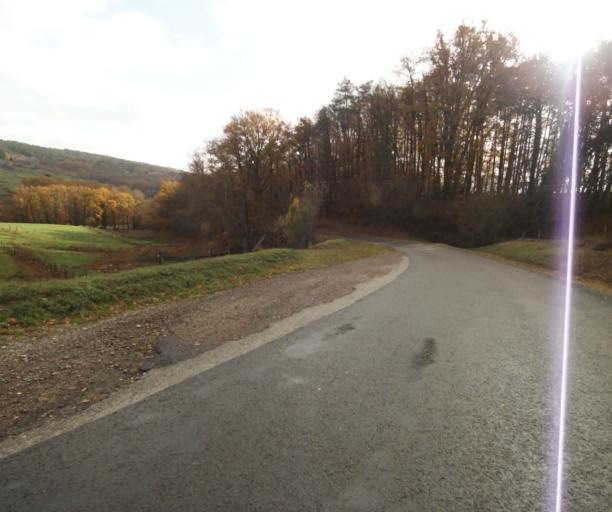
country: FR
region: Limousin
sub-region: Departement de la Correze
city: Saint-Mexant
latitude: 45.2363
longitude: 1.6382
